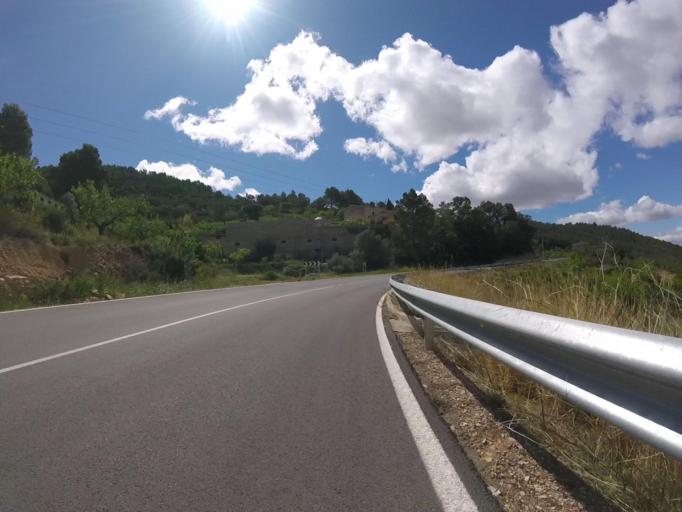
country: ES
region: Valencia
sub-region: Provincia de Castello
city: Culla
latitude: 40.2779
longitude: -0.1113
